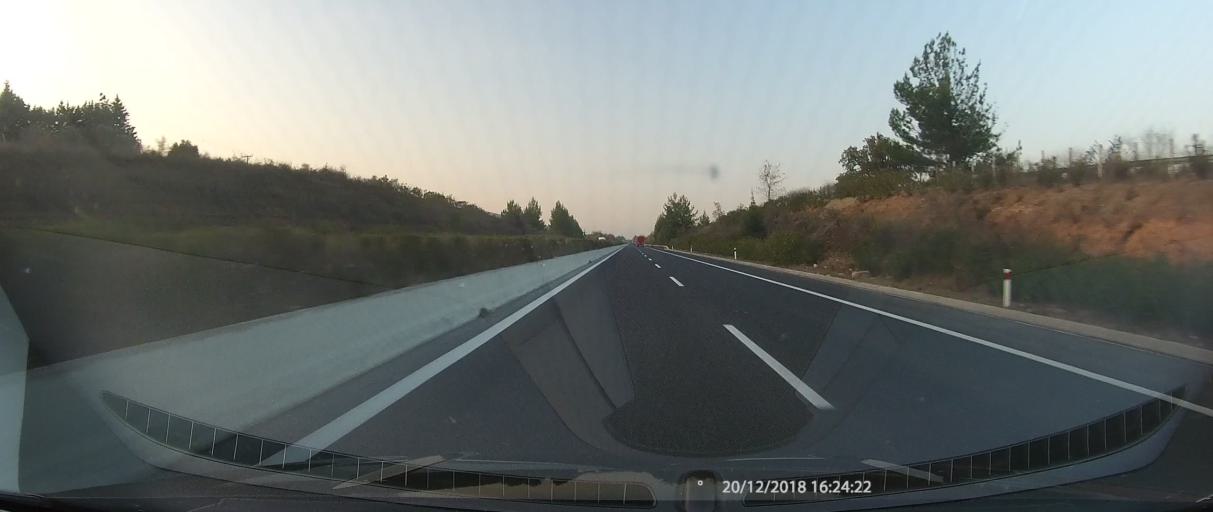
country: GR
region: Thessaly
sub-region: Nomos Magnisias
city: Sourpi
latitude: 39.1079
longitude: 22.8601
